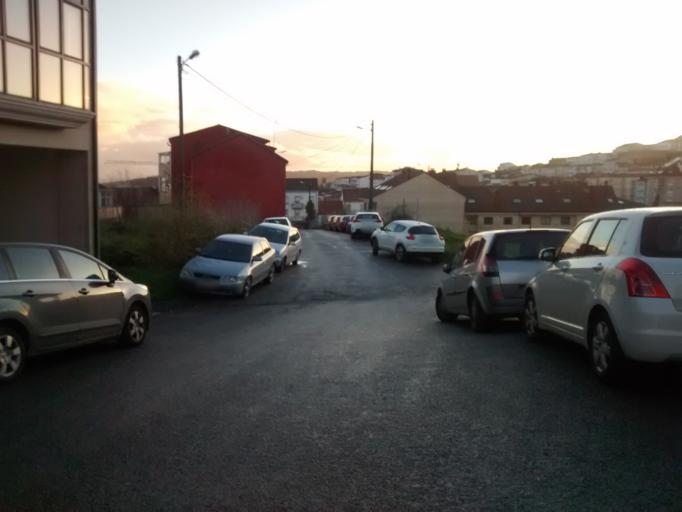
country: ES
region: Galicia
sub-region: Provincia da Coruna
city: Santiago de Compostela
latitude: 42.8861
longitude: -8.5315
